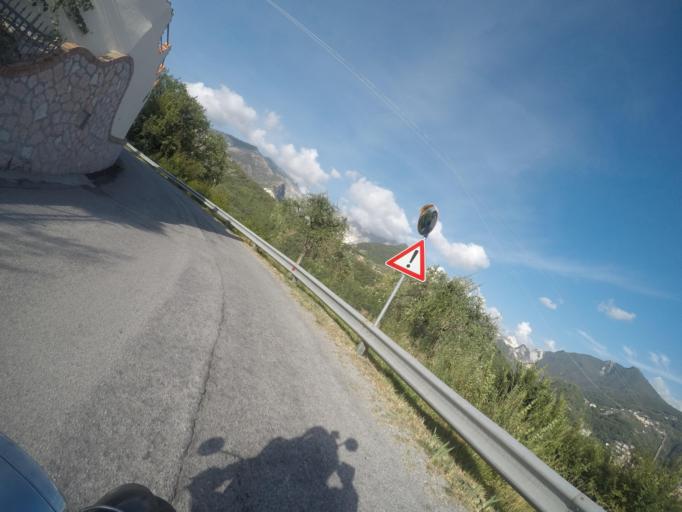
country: IT
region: Tuscany
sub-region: Provincia di Massa-Carrara
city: Carrara
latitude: 44.0843
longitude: 10.0917
